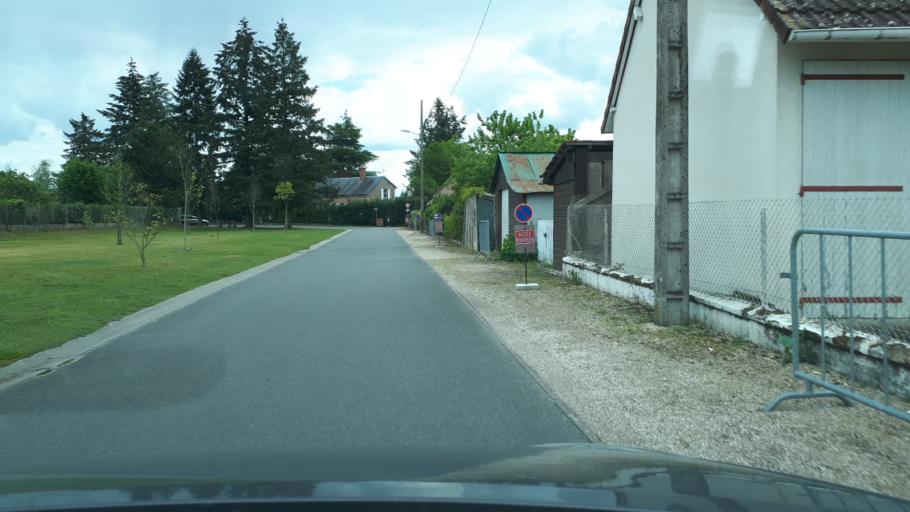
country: FR
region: Centre
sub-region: Departement du Loir-et-Cher
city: Souesmes
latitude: 47.5110
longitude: 2.1507
